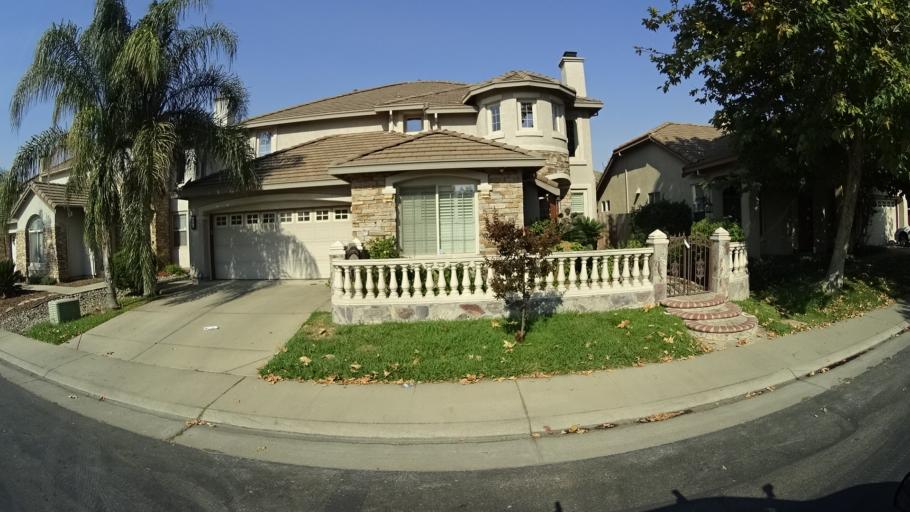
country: US
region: California
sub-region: Sacramento County
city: Laguna
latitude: 38.3929
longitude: -121.4326
